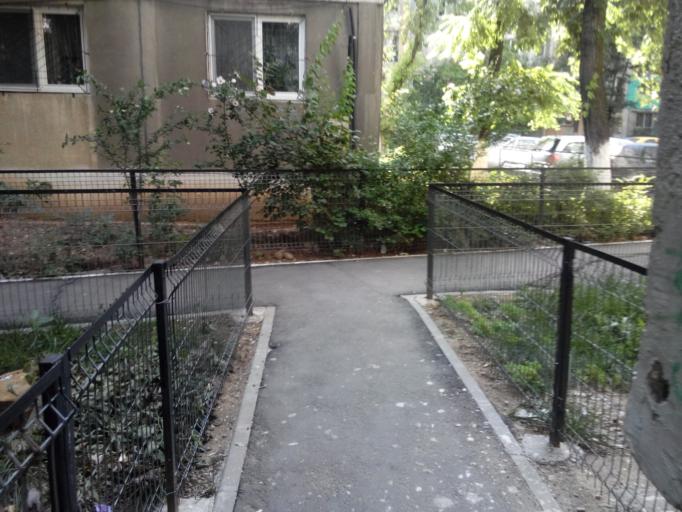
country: RO
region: Ilfov
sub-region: Comuna Chiajna
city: Rosu
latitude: 44.4333
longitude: 26.0269
